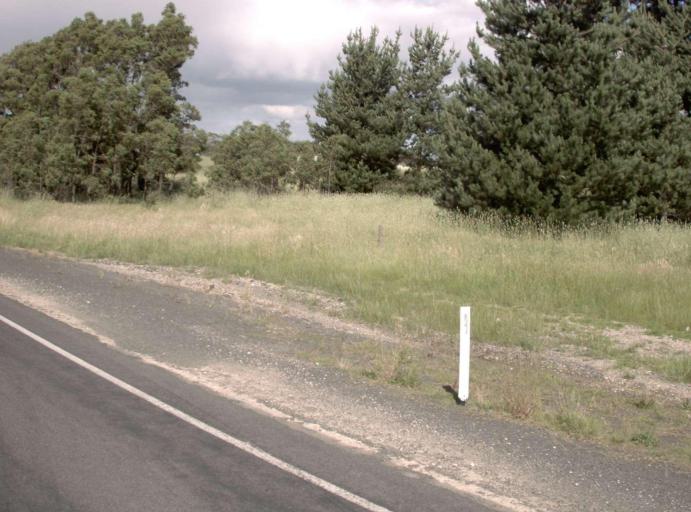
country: AU
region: Victoria
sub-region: Latrobe
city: Traralgon
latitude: -38.1375
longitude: 146.5386
